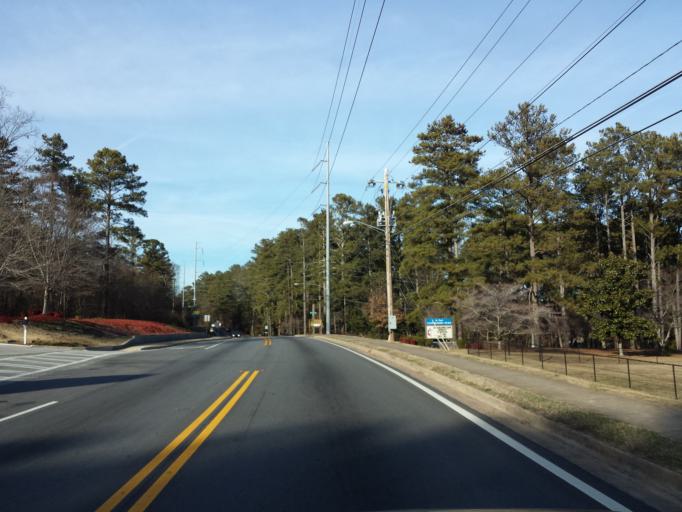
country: US
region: Georgia
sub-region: Cobb County
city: Marietta
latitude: 34.0020
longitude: -84.5454
